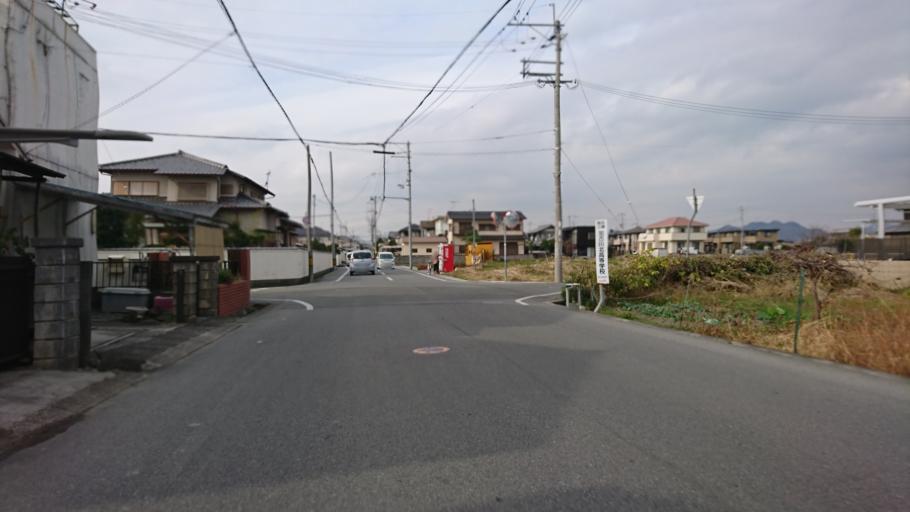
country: JP
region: Hyogo
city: Kakogawacho-honmachi
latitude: 34.7659
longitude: 134.8561
